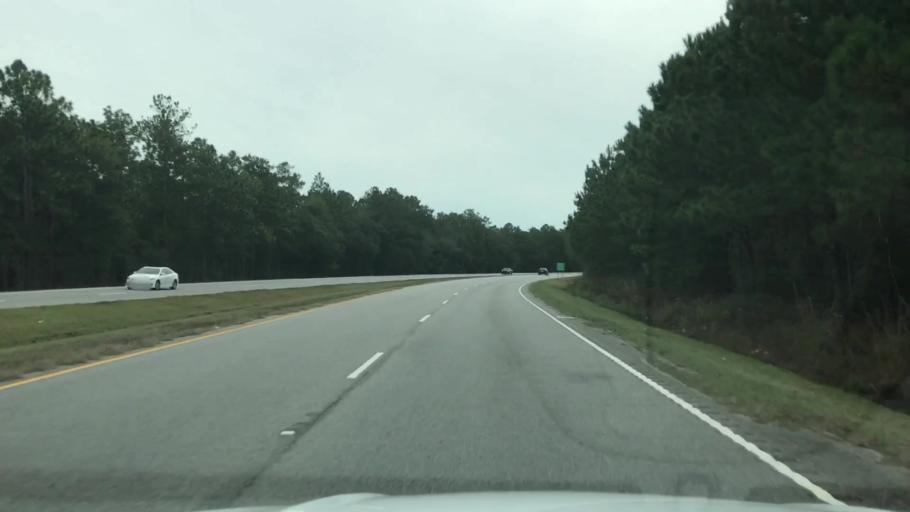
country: US
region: South Carolina
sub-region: Georgetown County
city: Georgetown
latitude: 33.3863
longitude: -79.2052
